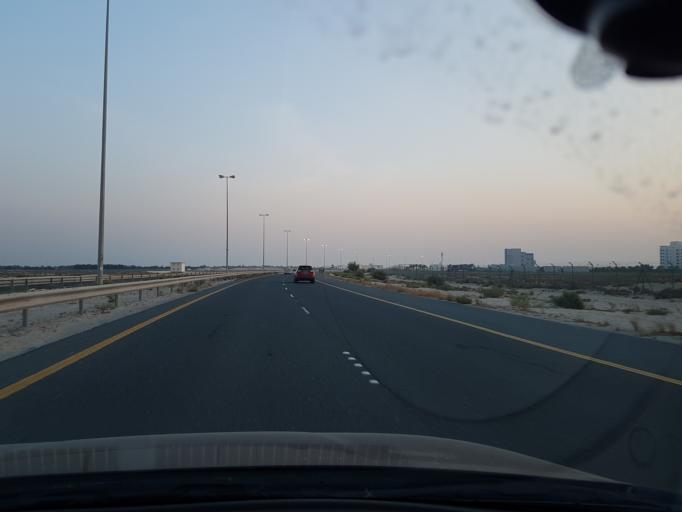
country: BH
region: Central Governorate
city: Dar Kulayb
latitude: 26.0325
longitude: 50.4996
